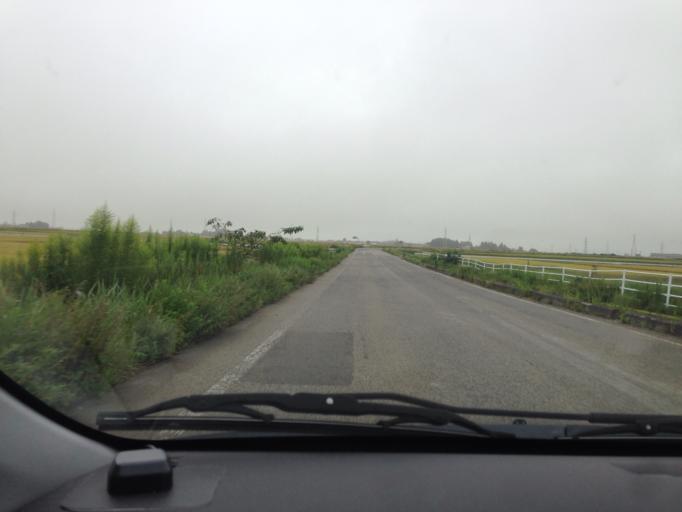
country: JP
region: Fukushima
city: Kitakata
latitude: 37.5851
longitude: 139.8699
